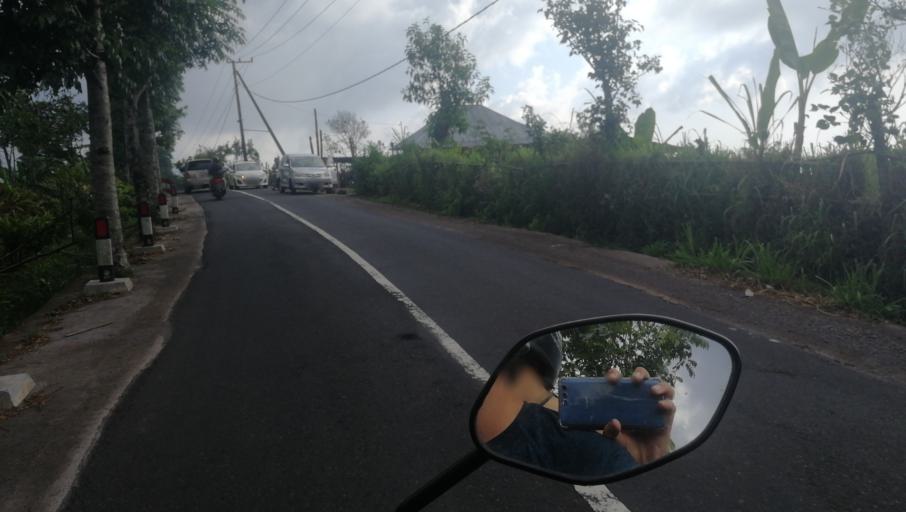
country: ID
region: Bali
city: Munduk
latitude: -8.2597
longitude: 115.0892
